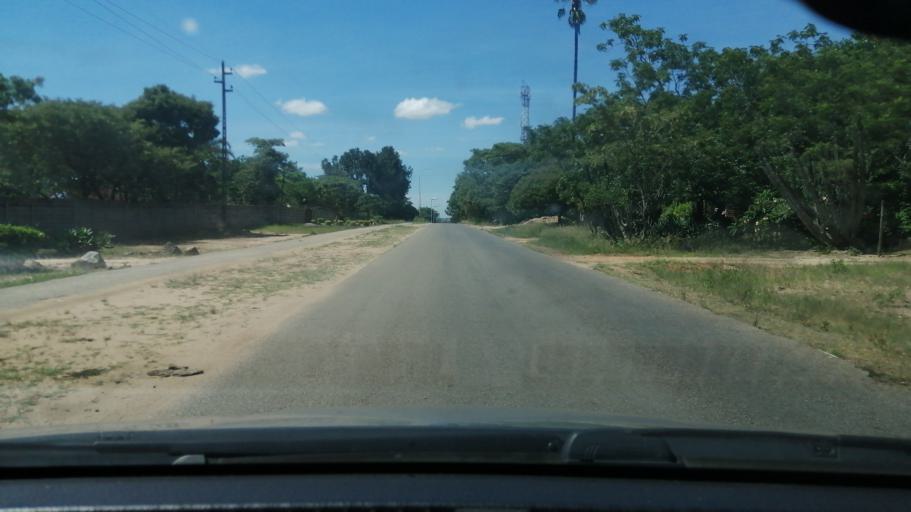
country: ZW
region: Harare
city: Epworth
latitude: -17.8251
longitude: 31.1257
